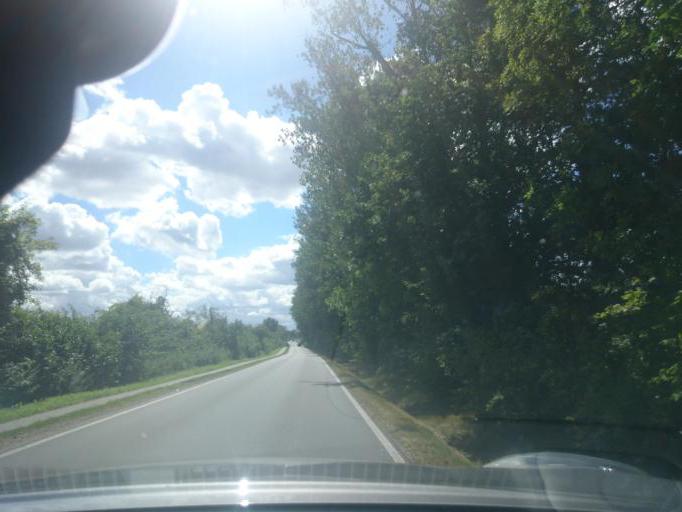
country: DE
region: Mecklenburg-Vorpommern
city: Lambrechtshagen
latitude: 54.1295
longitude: 12.0335
